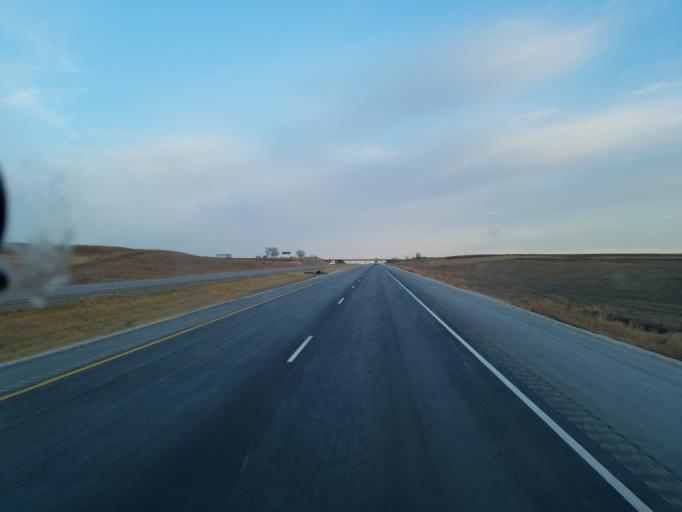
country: US
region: Iowa
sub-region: Harrison County
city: Logan
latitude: 41.4989
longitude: -95.7167
